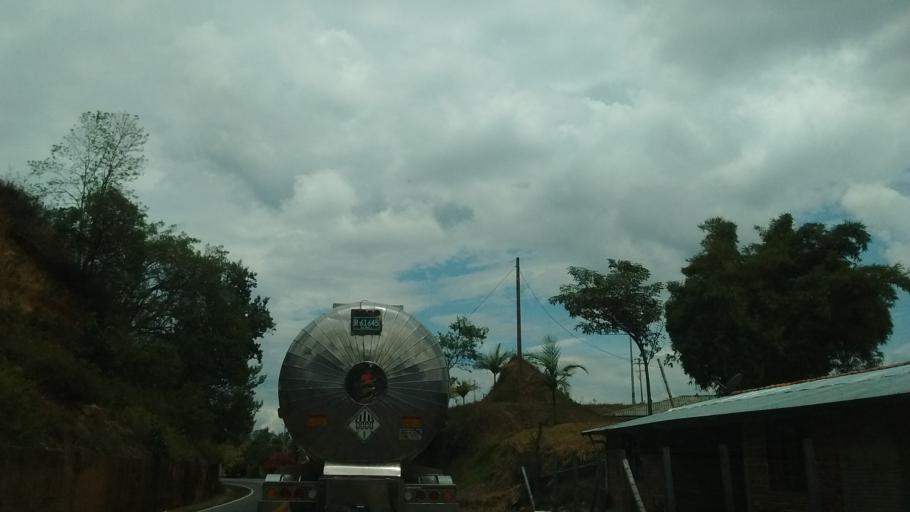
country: CO
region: Cauca
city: Rosas
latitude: 2.3056
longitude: -76.7037
